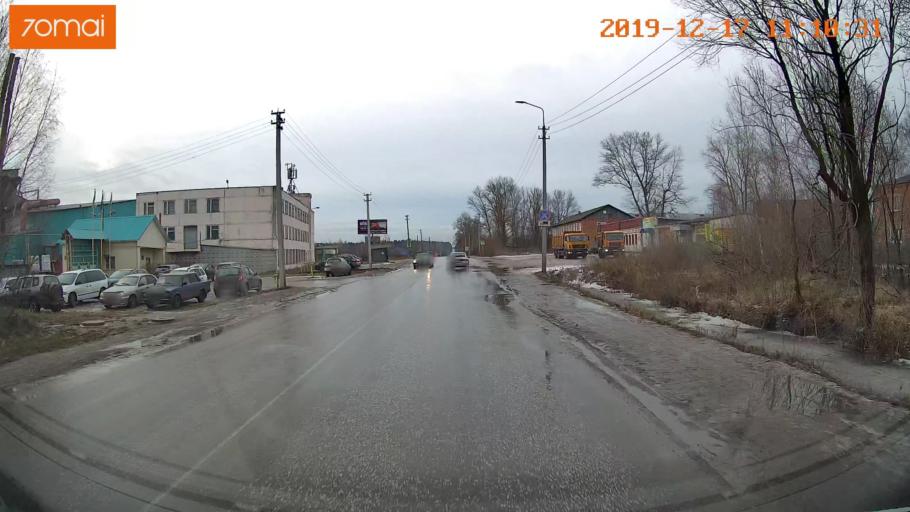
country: RU
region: Vladimir
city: Gus'-Khrustal'nyy
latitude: 55.5922
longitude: 40.6410
